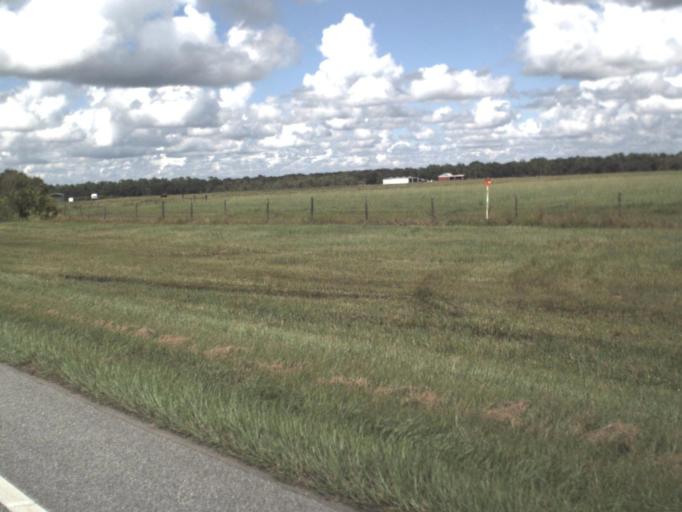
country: US
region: Florida
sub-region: DeSoto County
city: Arcadia
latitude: 27.3294
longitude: -82.1333
